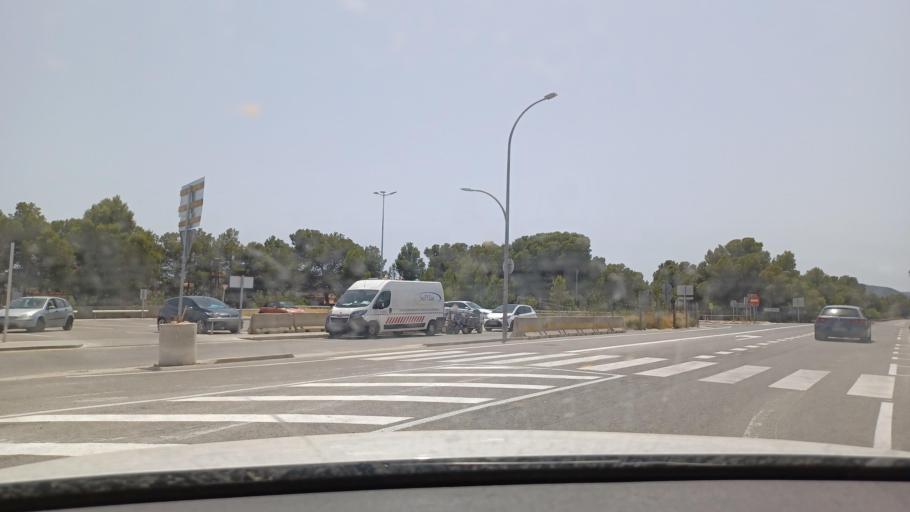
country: ES
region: Catalonia
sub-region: Provincia de Tarragona
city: Colldejou
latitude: 41.0005
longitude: 0.9295
